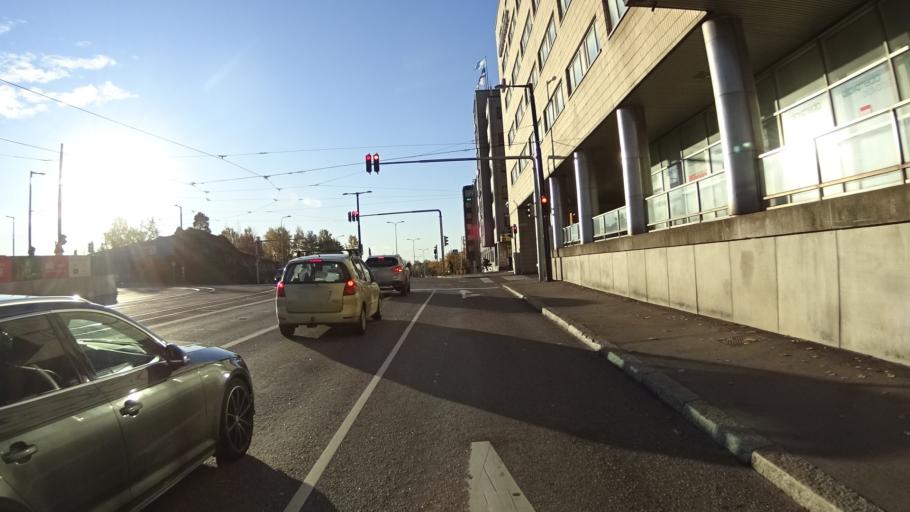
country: FI
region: Uusimaa
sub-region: Helsinki
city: Helsinki
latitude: 60.1978
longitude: 24.9280
